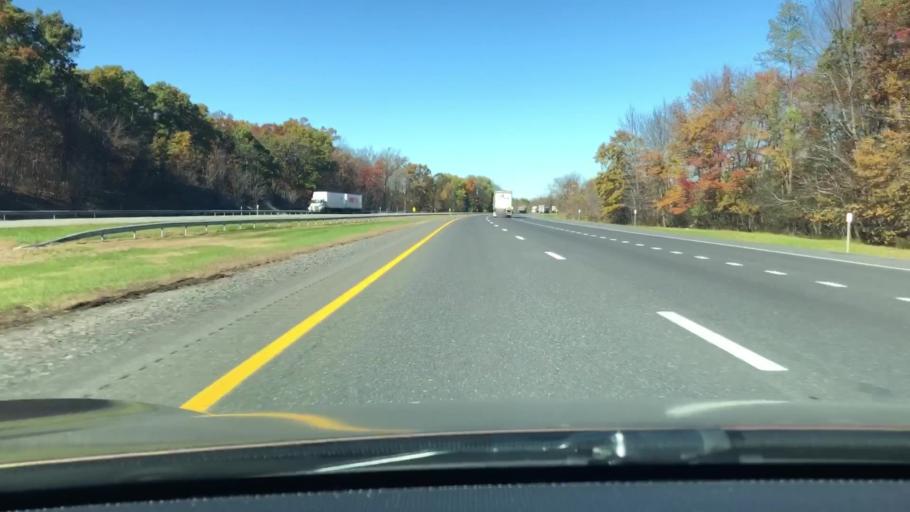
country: US
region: New York
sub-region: Ulster County
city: Plattekill
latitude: 41.5802
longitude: -74.0873
